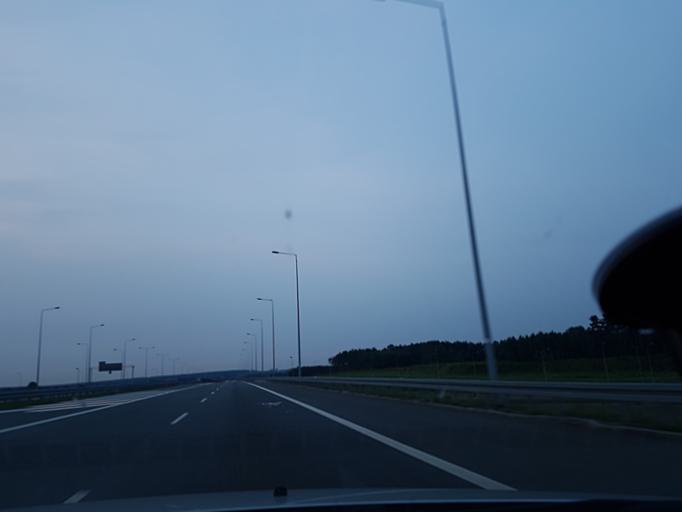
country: PL
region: Lodz Voivodeship
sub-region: Powiat zgierski
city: Strykow
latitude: 51.8907
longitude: 19.6357
